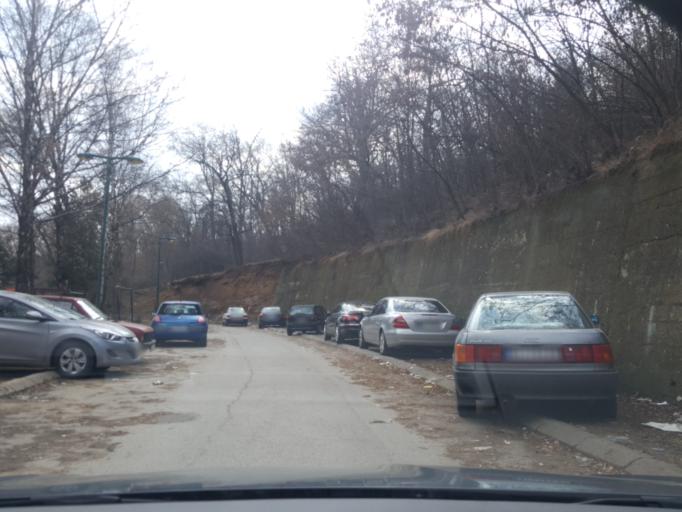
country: RS
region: Central Serbia
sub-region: Nisavski Okrug
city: Nis
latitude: 43.3138
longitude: 21.8643
